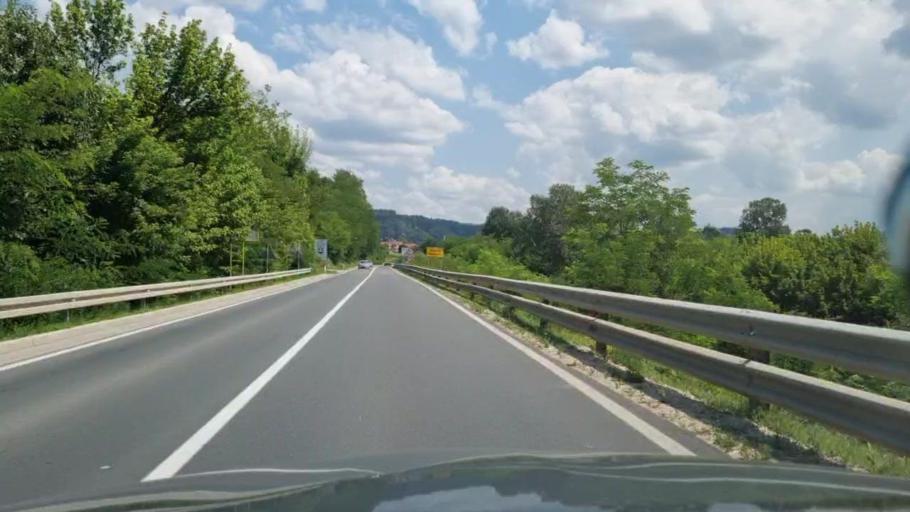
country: BA
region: Federation of Bosnia and Herzegovina
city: Gnojnica
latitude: 44.6155
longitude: 18.4136
